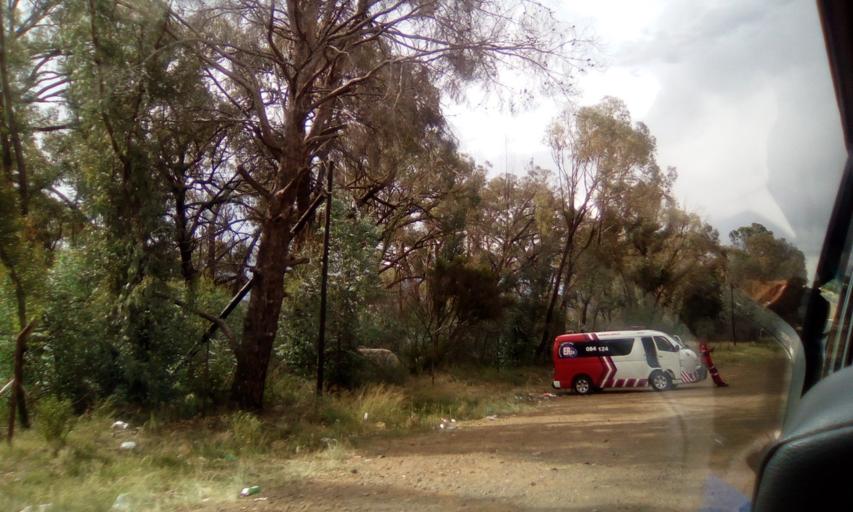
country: ZA
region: Orange Free State
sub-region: Thabo Mofutsanyana District Municipality
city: Ladybrand
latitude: -29.2085
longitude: 27.4670
